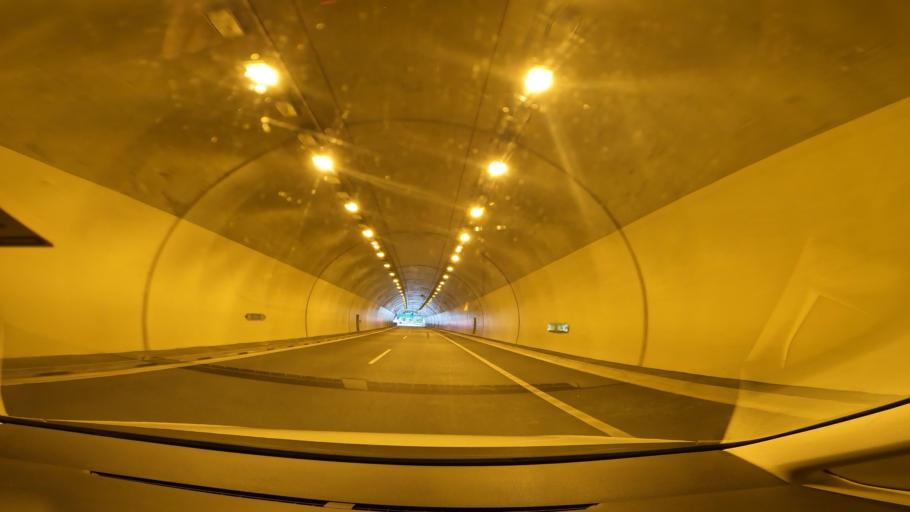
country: SI
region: Zetale
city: Zetale
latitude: 46.2807
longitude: 15.8607
